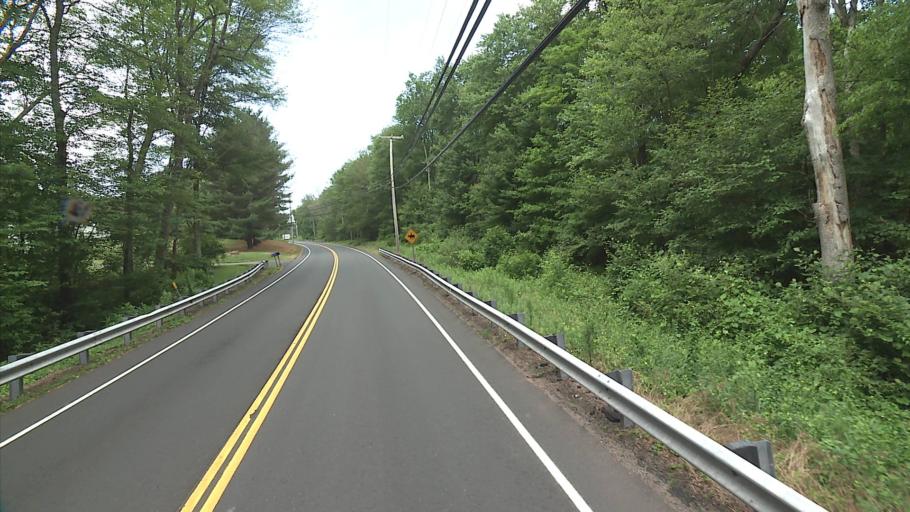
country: US
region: Connecticut
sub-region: Hartford County
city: Manchester
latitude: 41.7101
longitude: -72.5095
